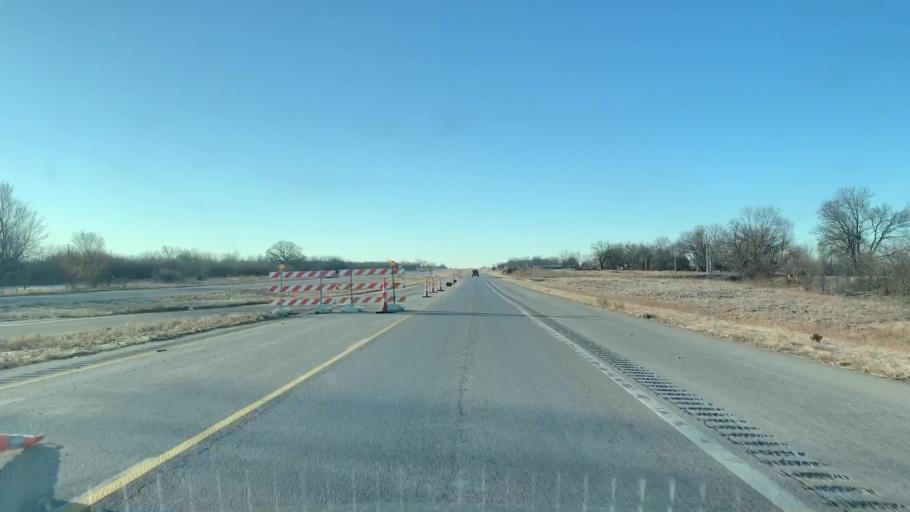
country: US
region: Kansas
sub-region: Bourbon County
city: Fort Scott
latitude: 37.7630
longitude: -94.7049
